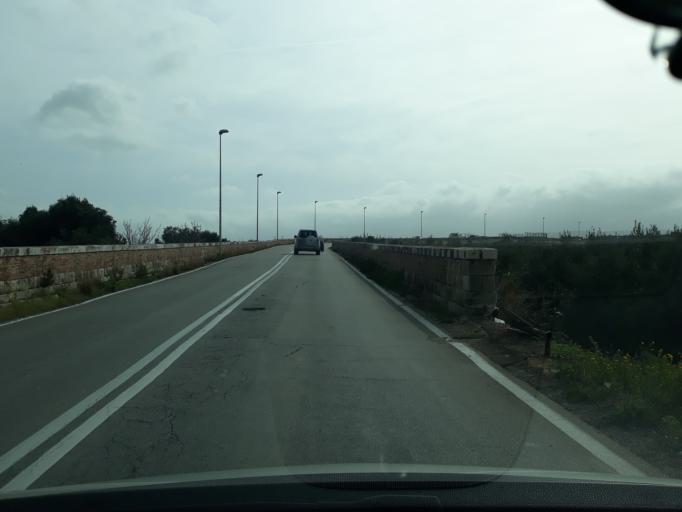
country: IT
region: Apulia
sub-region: Provincia di Bari
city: Monopoli
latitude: 40.9587
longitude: 17.2823
